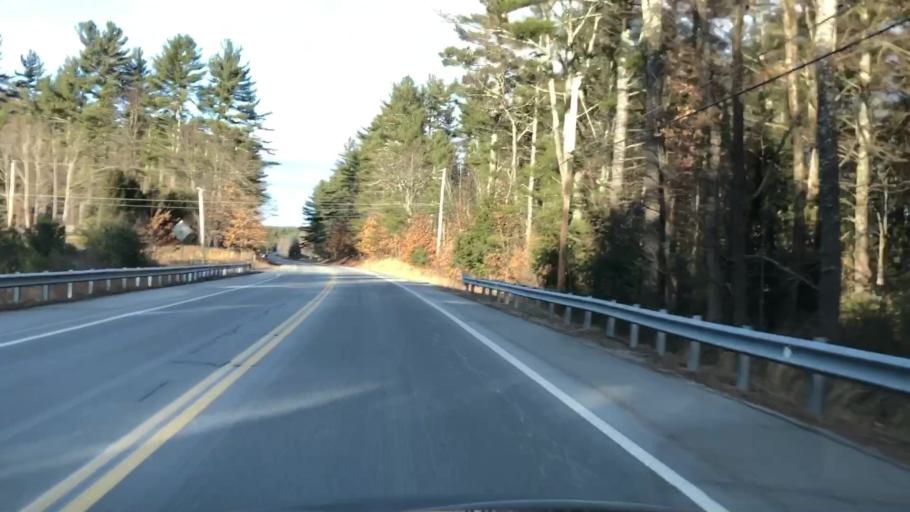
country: US
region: New Hampshire
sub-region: Hillsborough County
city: Brookline
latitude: 42.7163
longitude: -71.6626
